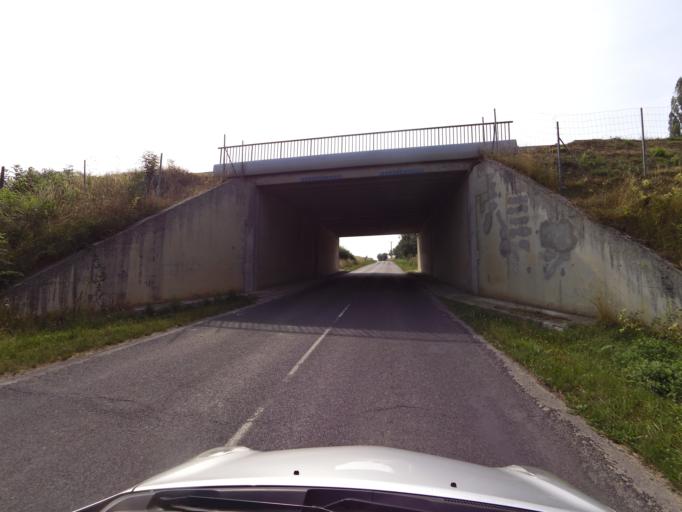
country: FR
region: Champagne-Ardenne
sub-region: Departement de la Marne
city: Jonchery-sur-Vesle
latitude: 49.2207
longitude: 3.8127
